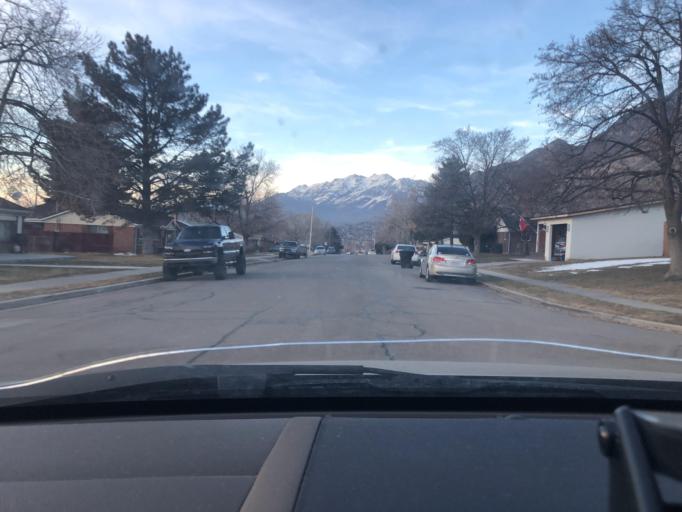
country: US
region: Utah
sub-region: Utah County
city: Provo
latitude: 40.2259
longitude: -111.6352
